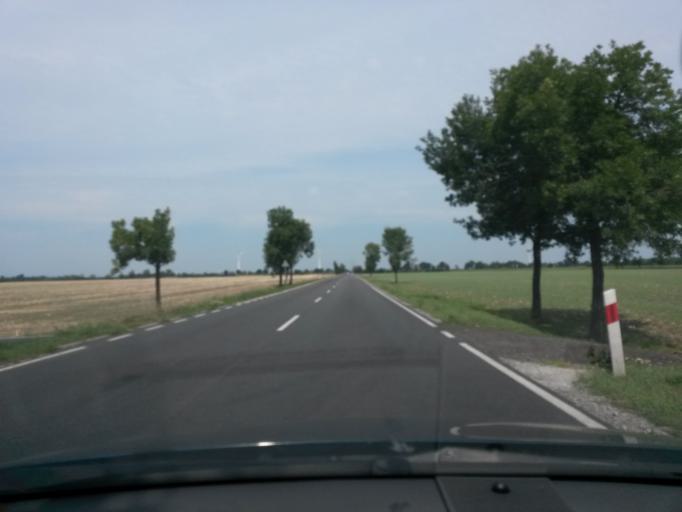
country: PL
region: Greater Poland Voivodeship
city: Miejska Gorka
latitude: 51.7042
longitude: 16.9470
